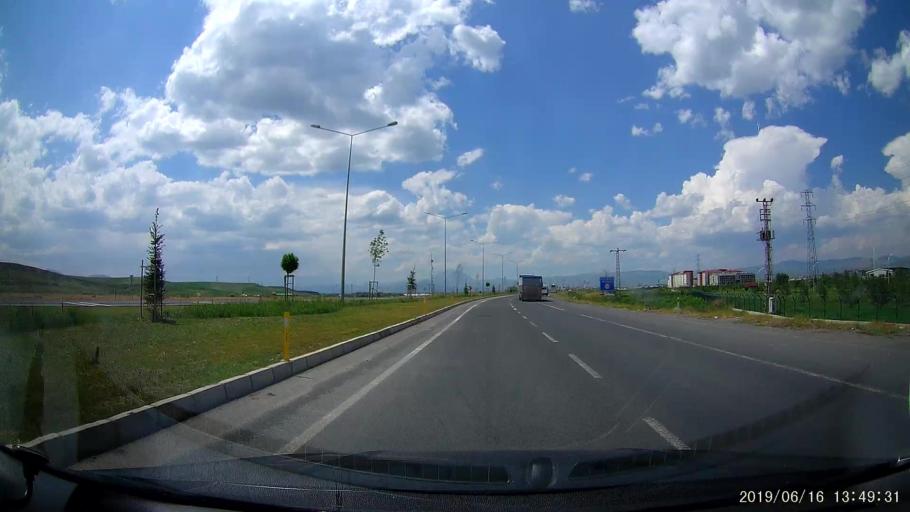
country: TR
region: Agri
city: Agri
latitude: 39.7180
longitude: 42.9896
